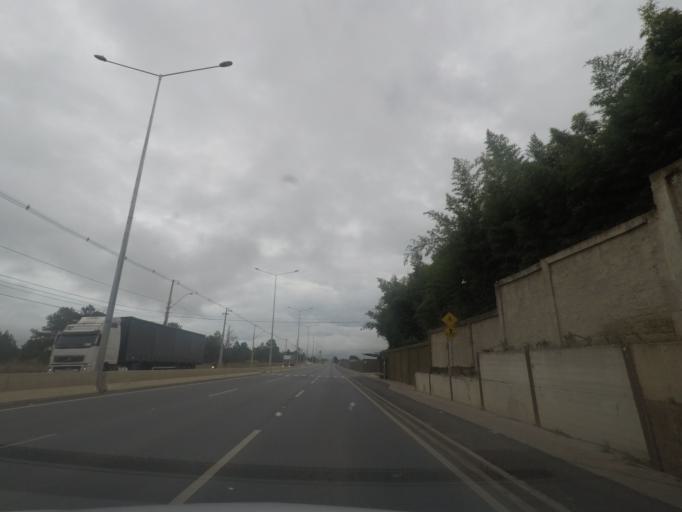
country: BR
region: Parana
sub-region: Piraquara
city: Piraquara
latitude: -25.4538
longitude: -49.1141
